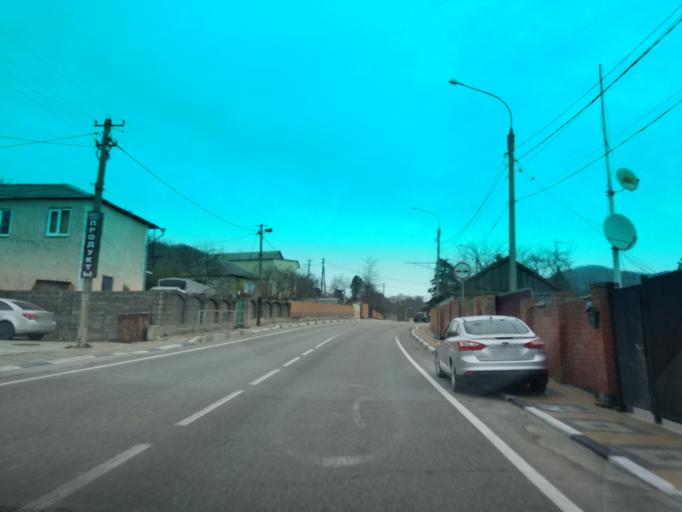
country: RU
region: Krasnodarskiy
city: Ol'ginka
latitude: 44.2098
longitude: 38.8922
